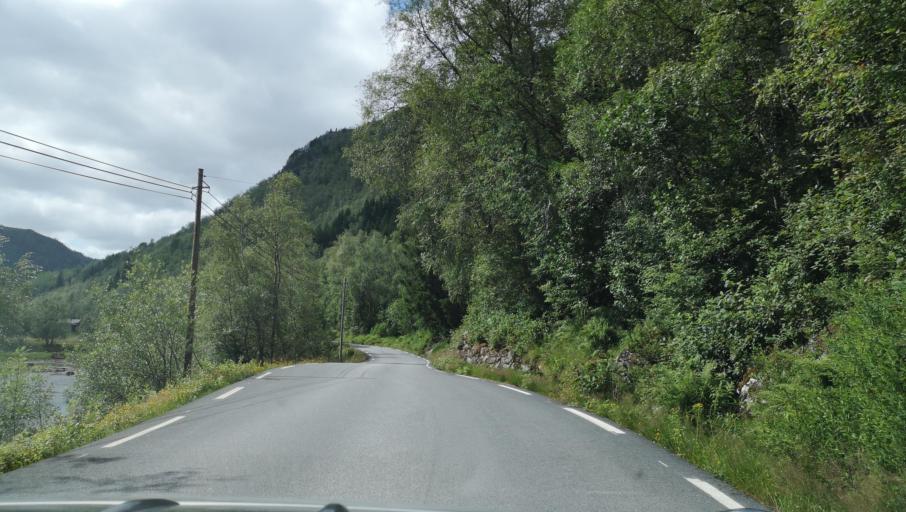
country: NO
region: Hordaland
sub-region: Modalen
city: Mo
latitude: 60.7861
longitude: 5.9401
